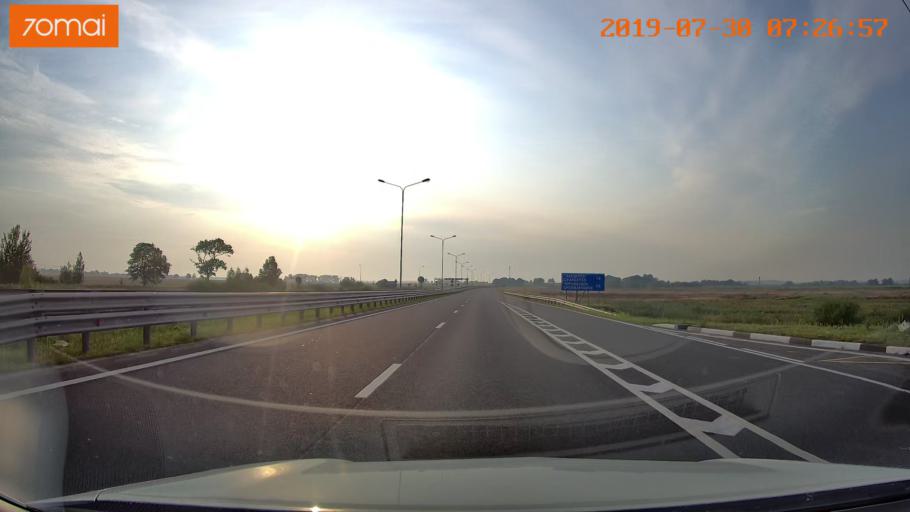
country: RU
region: Kaliningrad
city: Gvardeysk
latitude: 54.6837
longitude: 20.8745
